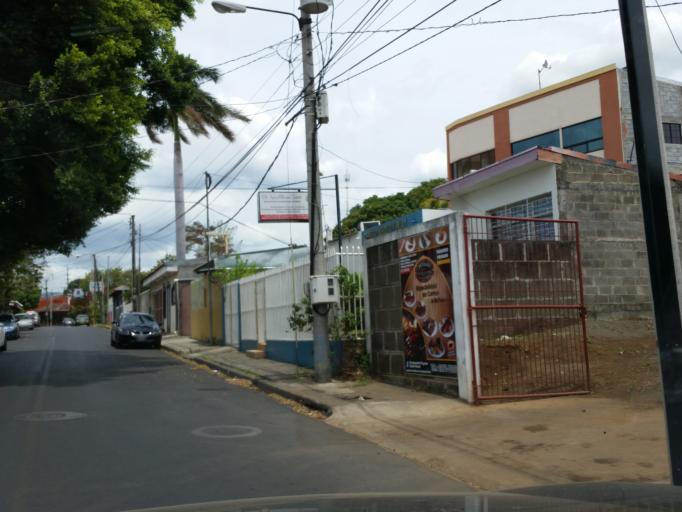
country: NI
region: Managua
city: Managua
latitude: 12.1177
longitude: -86.2551
